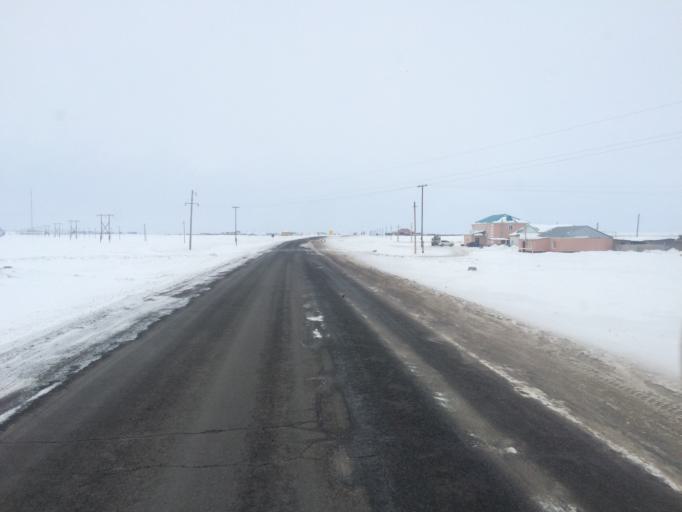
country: RU
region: Orenburg
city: Dombarovskiy
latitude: 49.9586
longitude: 60.0817
